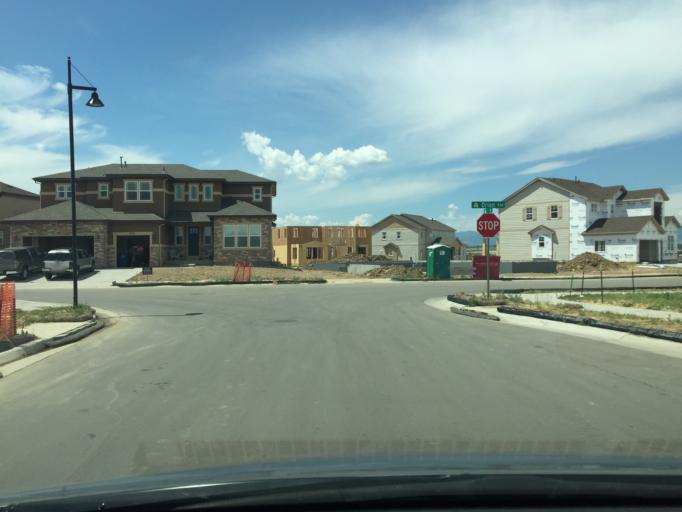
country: US
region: Colorado
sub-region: Boulder County
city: Erie
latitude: 40.0496
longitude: -105.0346
